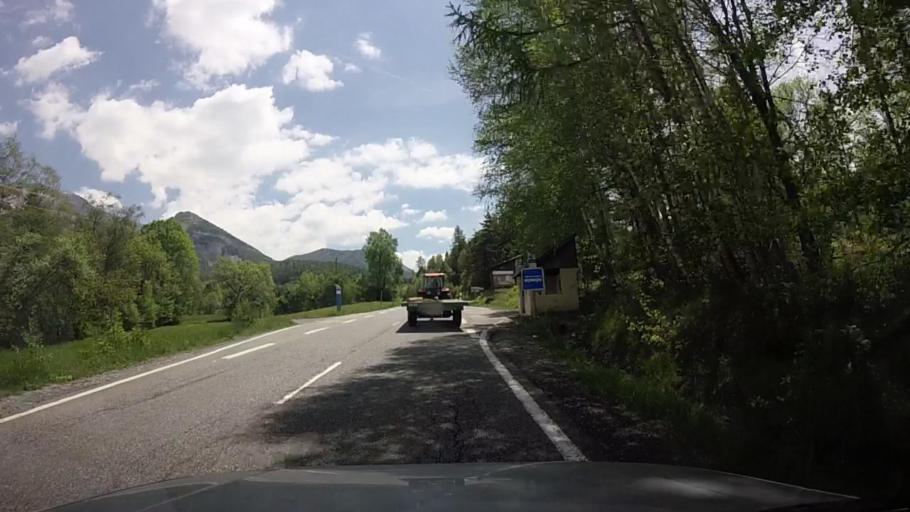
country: FR
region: Provence-Alpes-Cote d'Azur
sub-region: Departement des Alpes-de-Haute-Provence
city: Seyne-les-Alpes
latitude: 44.3232
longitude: 6.3981
